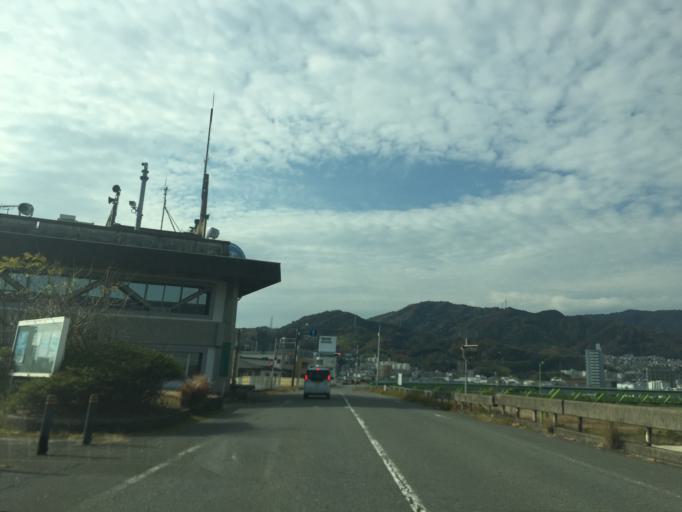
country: JP
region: Hiroshima
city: Hiroshima-shi
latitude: 34.4244
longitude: 132.4630
